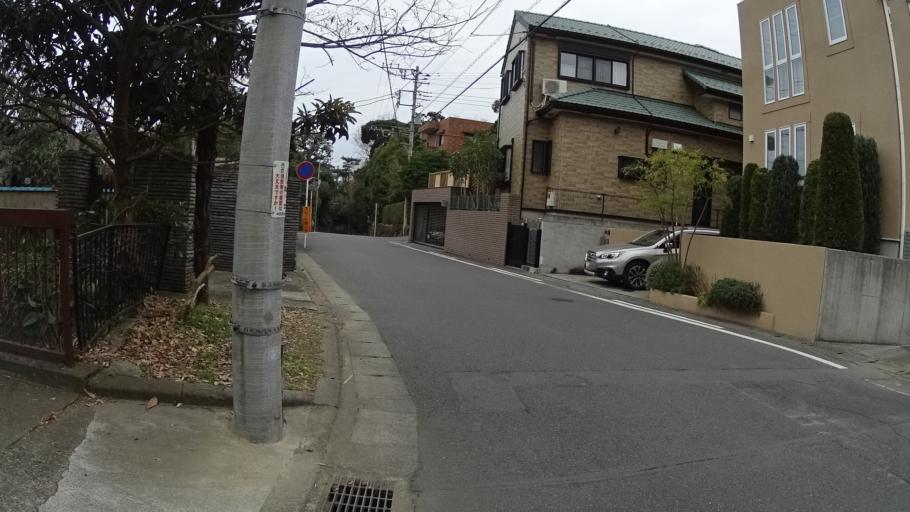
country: JP
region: Kanagawa
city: Oiso
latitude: 35.3120
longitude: 139.3077
